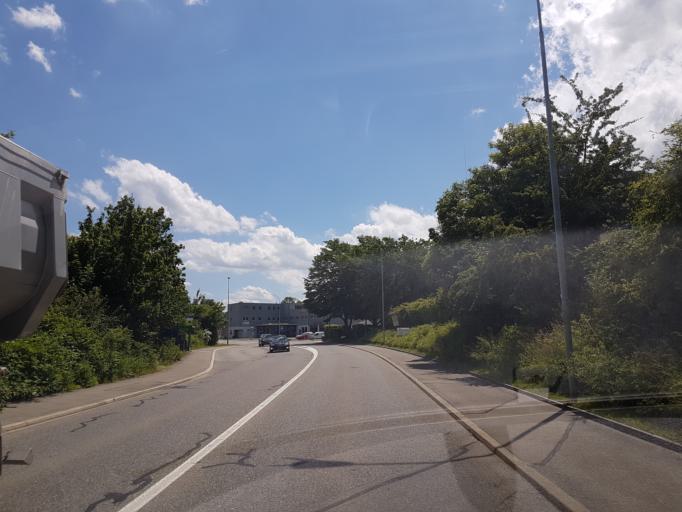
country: CH
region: Aargau
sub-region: Bezirk Baden
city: Mellingen
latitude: 47.4137
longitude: 8.2744
